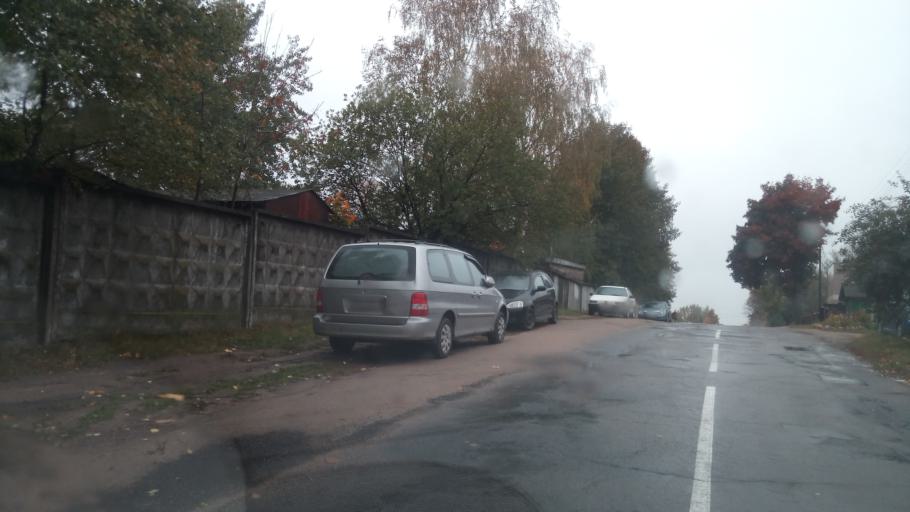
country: BY
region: Minsk
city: Minsk
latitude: 53.9391
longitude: 27.5923
